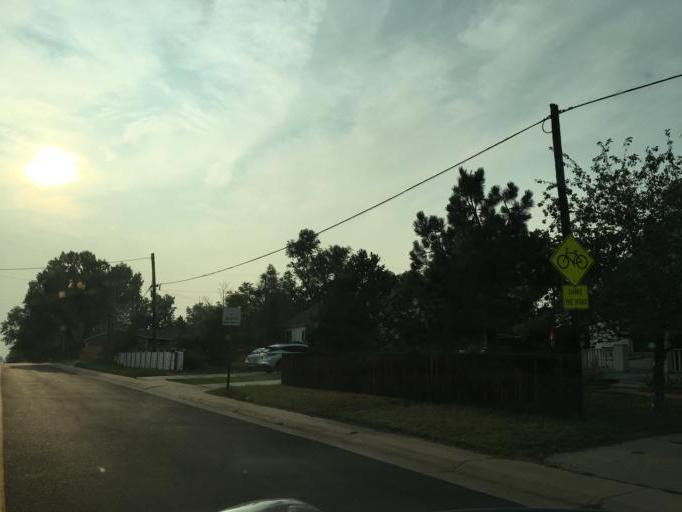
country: US
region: Colorado
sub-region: Arapahoe County
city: Glendale
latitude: 39.6894
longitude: -104.9327
